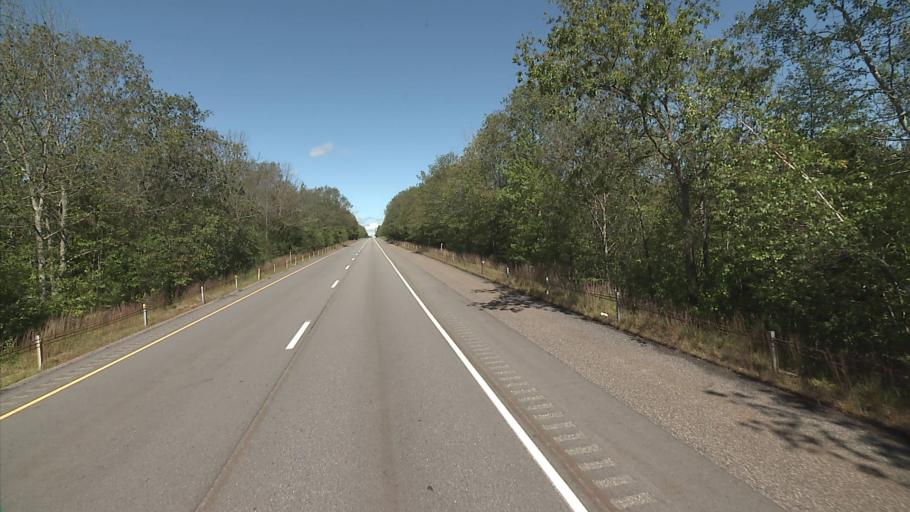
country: US
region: Connecticut
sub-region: New London County
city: Colchester
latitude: 41.5302
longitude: -72.3077
